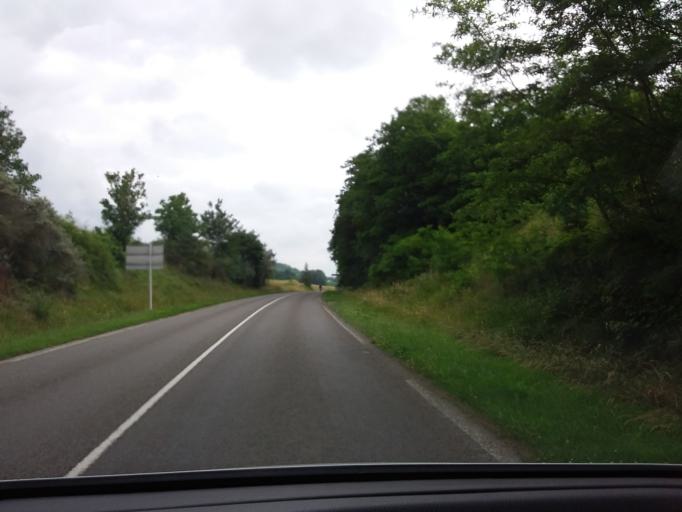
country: FR
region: Picardie
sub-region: Departement de l'Aisne
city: Bucy-le-Long
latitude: 49.3881
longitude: 3.4448
